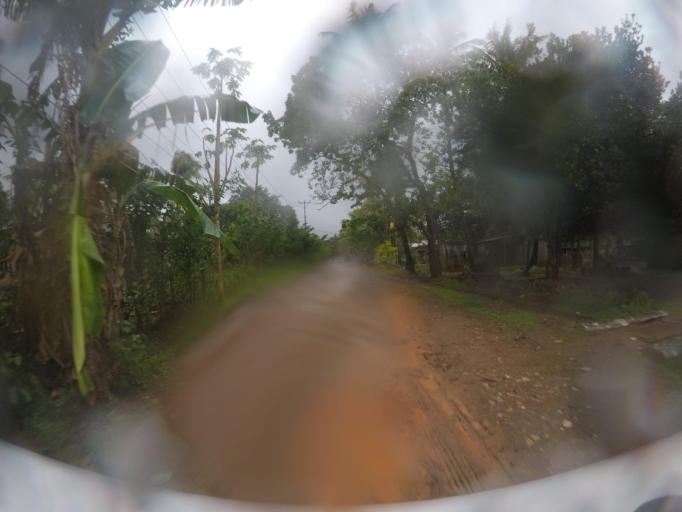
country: TL
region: Bobonaro
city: Maliana
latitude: -8.9669
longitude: 125.2160
